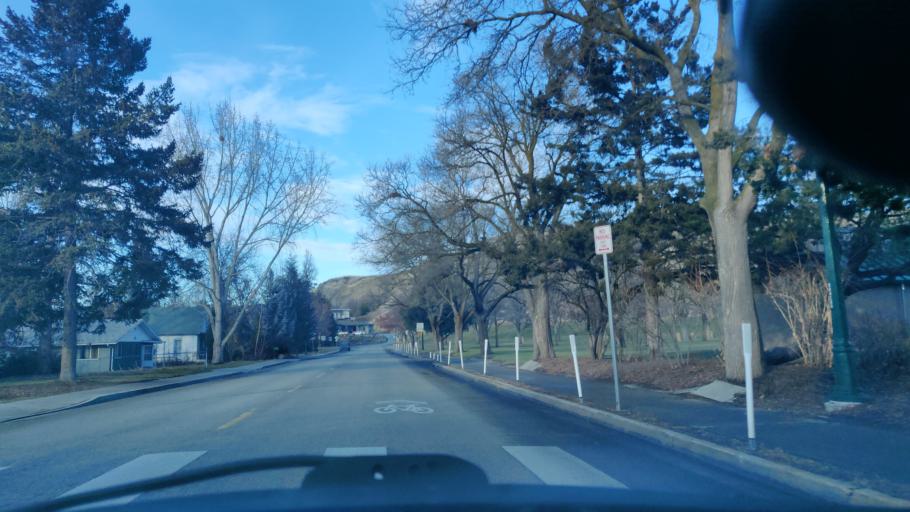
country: US
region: Idaho
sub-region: Ada County
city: Boise
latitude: 43.6346
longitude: -116.2033
